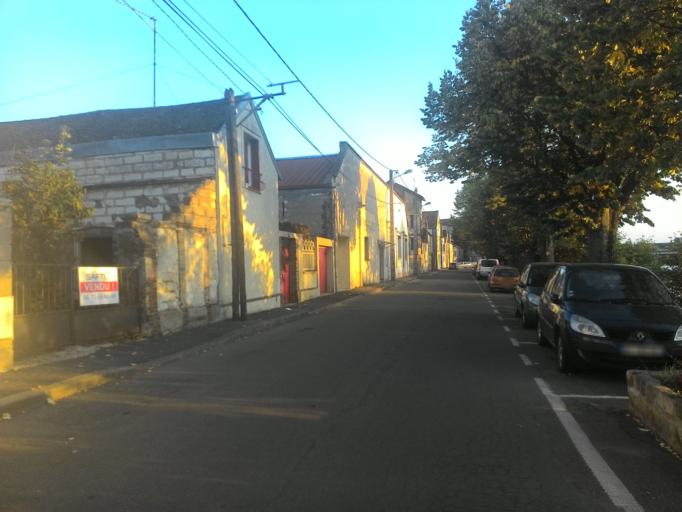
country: FR
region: Bourgogne
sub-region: Departement de l'Yonne
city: Sens
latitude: 48.1997
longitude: 3.2740
